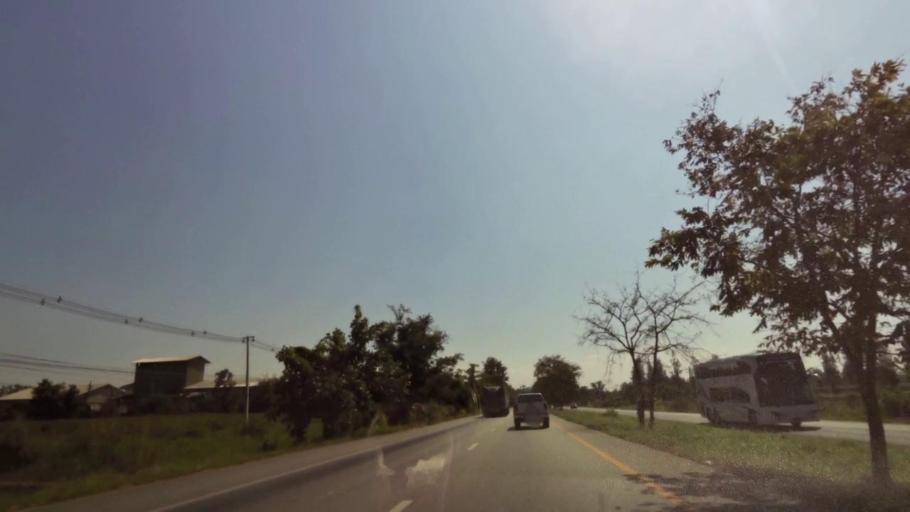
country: TH
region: Nakhon Sawan
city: Kao Liao
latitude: 15.8170
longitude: 100.1196
